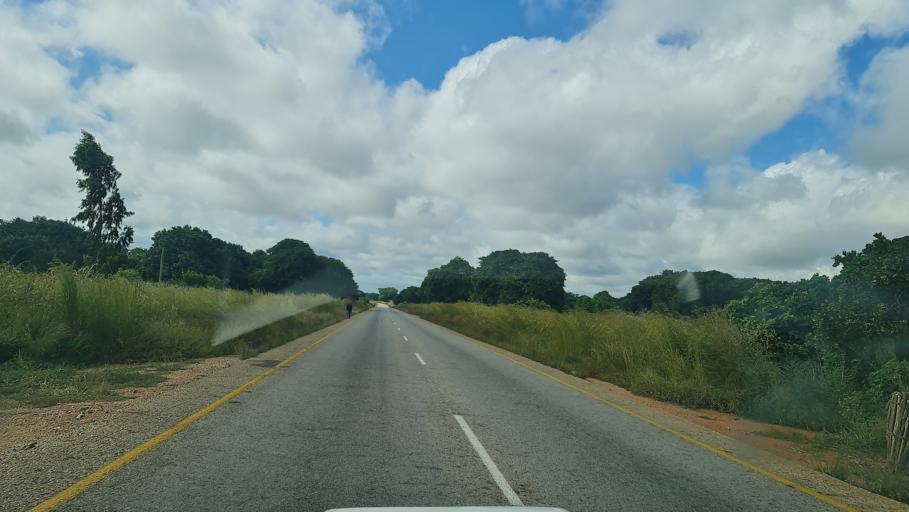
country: MZ
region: Nampula
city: Nampula
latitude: -15.0820
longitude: 39.5189
